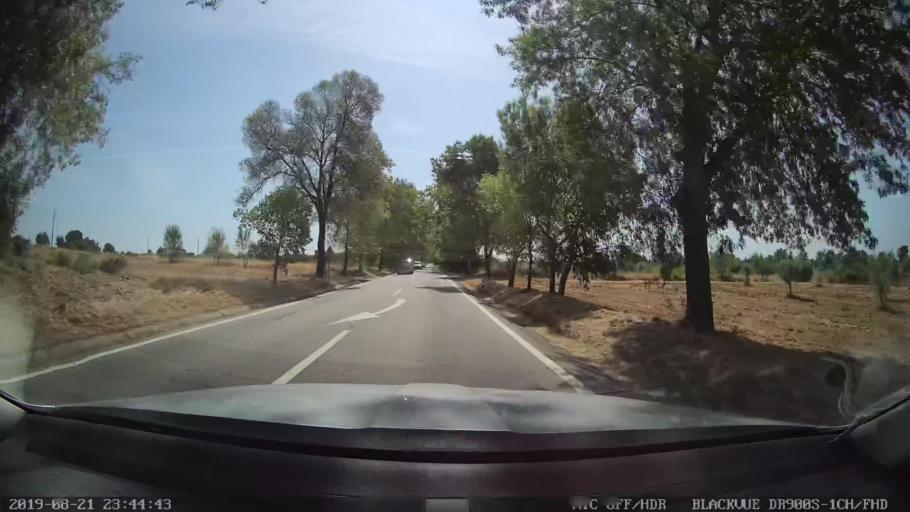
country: PT
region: Castelo Branco
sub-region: Idanha-A-Nova
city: Idanha-a-Nova
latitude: 39.8450
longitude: -7.2745
